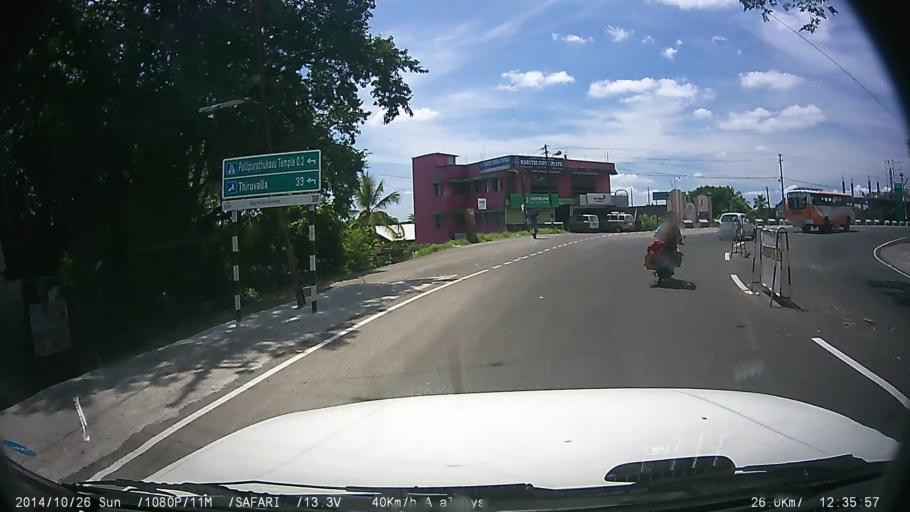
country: IN
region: Kerala
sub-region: Kottayam
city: Kottayam
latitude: 9.5817
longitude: 76.5232
